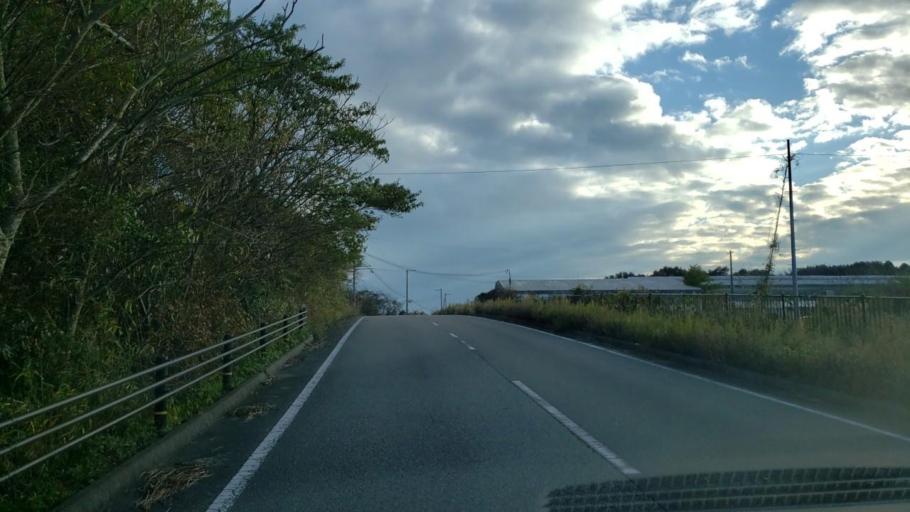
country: JP
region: Hyogo
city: Akashi
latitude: 34.5595
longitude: 134.9750
